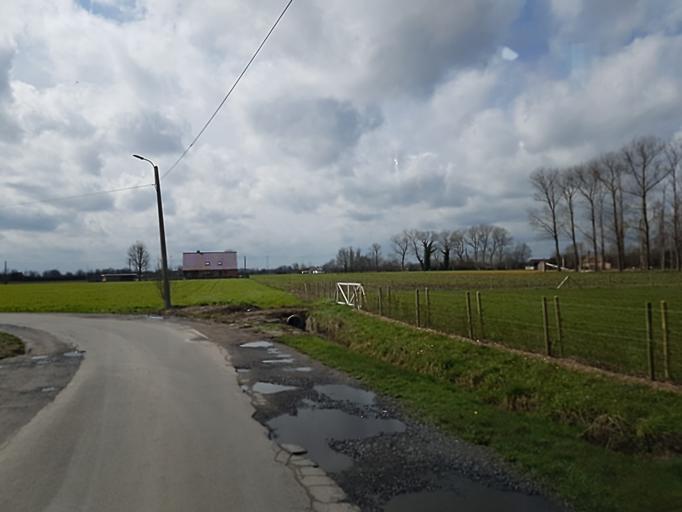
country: BE
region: Flanders
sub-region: Provincie Oost-Vlaanderen
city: Kruishoutem
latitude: 50.9404
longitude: 3.4994
